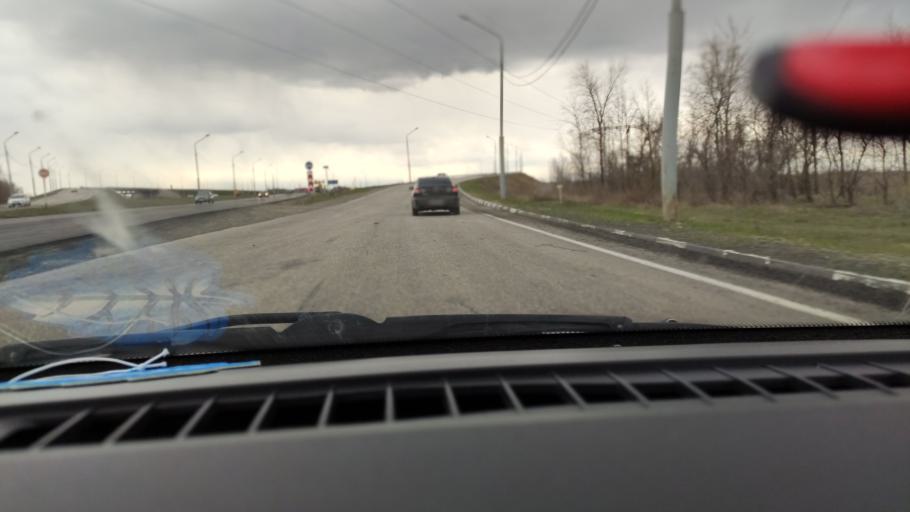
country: RU
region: Saratov
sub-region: Saratovskiy Rayon
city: Saratov
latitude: 51.6687
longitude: 45.9984
